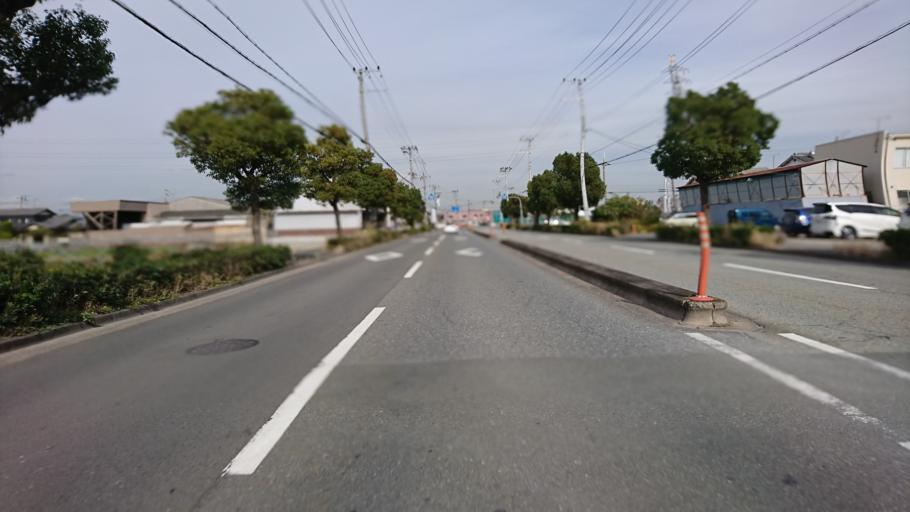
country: JP
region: Hyogo
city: Kakogawacho-honmachi
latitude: 34.7452
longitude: 134.8161
